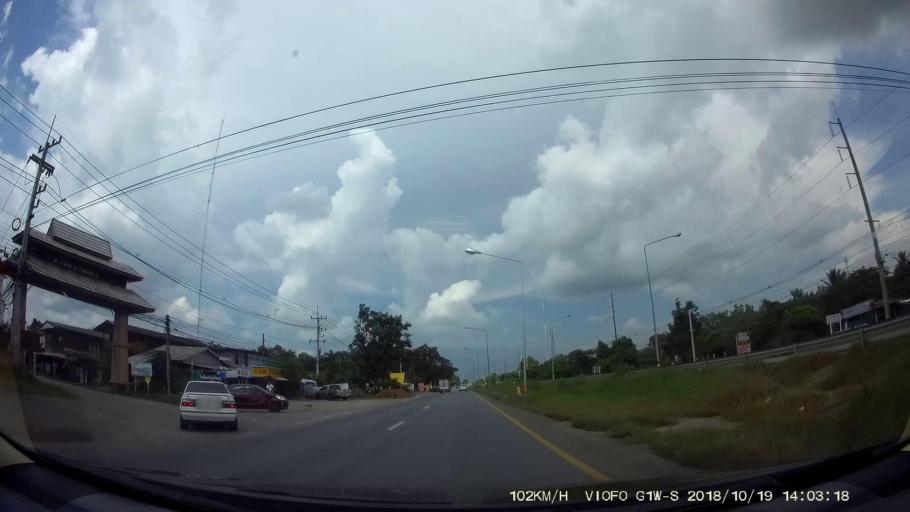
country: TH
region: Chaiyaphum
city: Chaiyaphum
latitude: 15.8510
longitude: 102.0690
